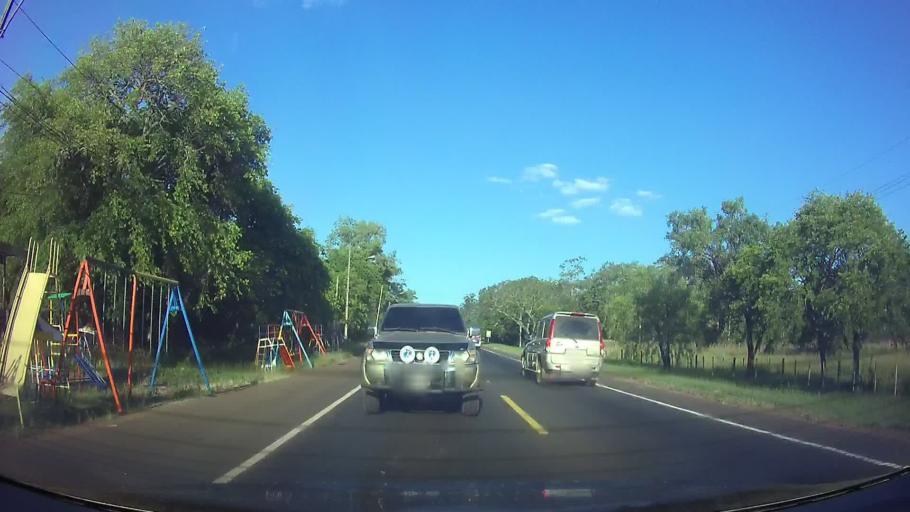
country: PY
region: Central
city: Ypacarai
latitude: -25.3765
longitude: -57.2333
